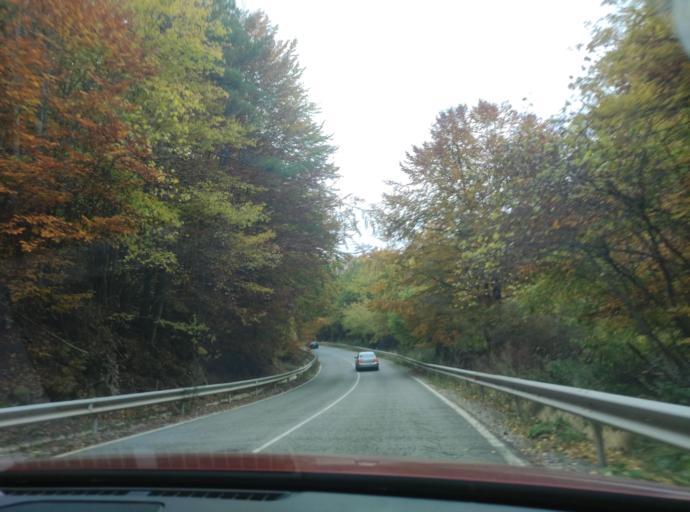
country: BG
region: Sofiya
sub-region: Obshtina Godech
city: Godech
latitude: 43.0238
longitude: 23.1371
